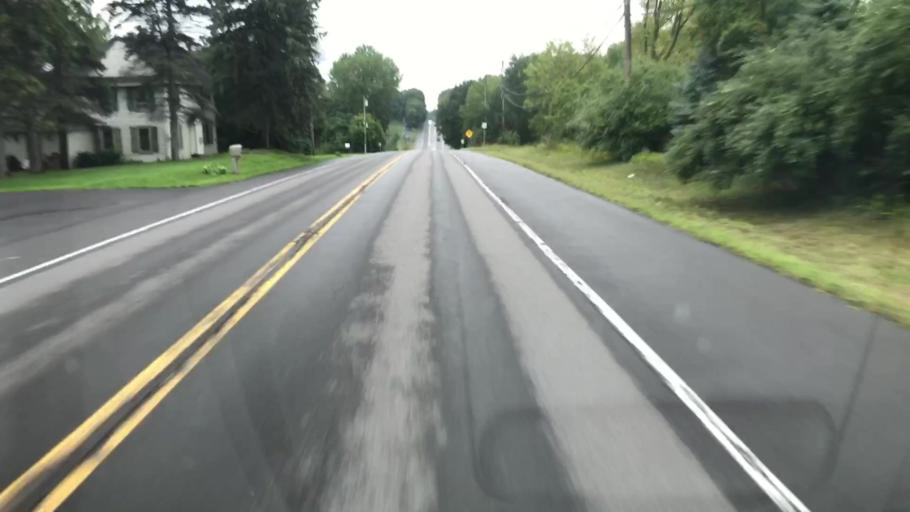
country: US
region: New York
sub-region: Cayuga County
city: Melrose Park
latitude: 42.9390
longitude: -76.5025
